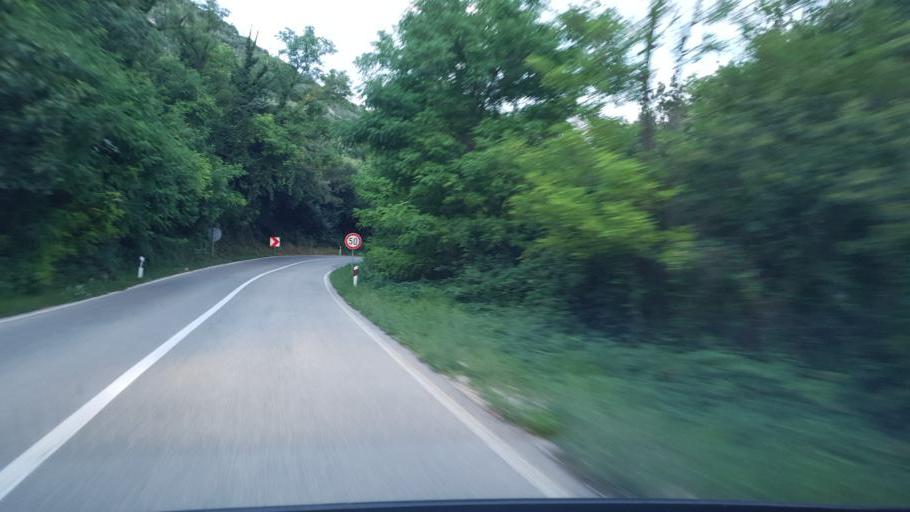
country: HR
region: Primorsko-Goranska
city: Punat
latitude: 45.0153
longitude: 14.6966
